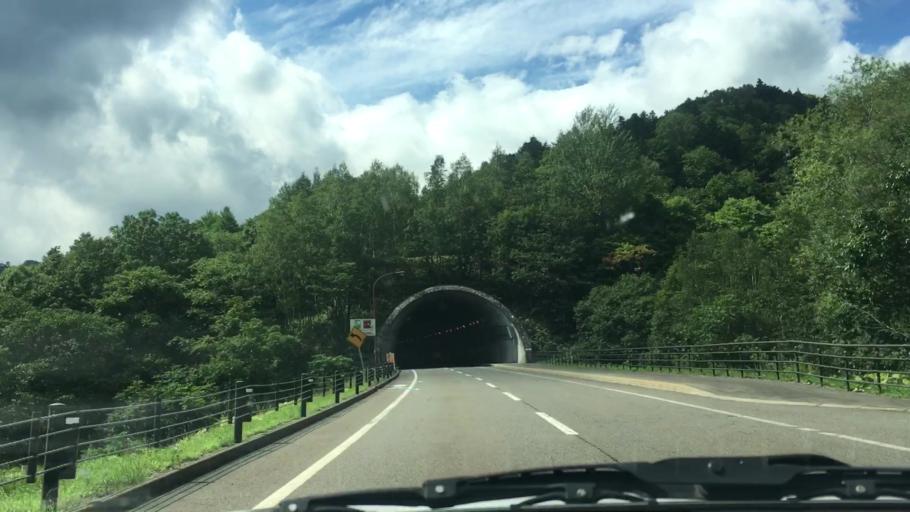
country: JP
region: Hokkaido
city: Otofuke
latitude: 43.3704
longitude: 143.2282
